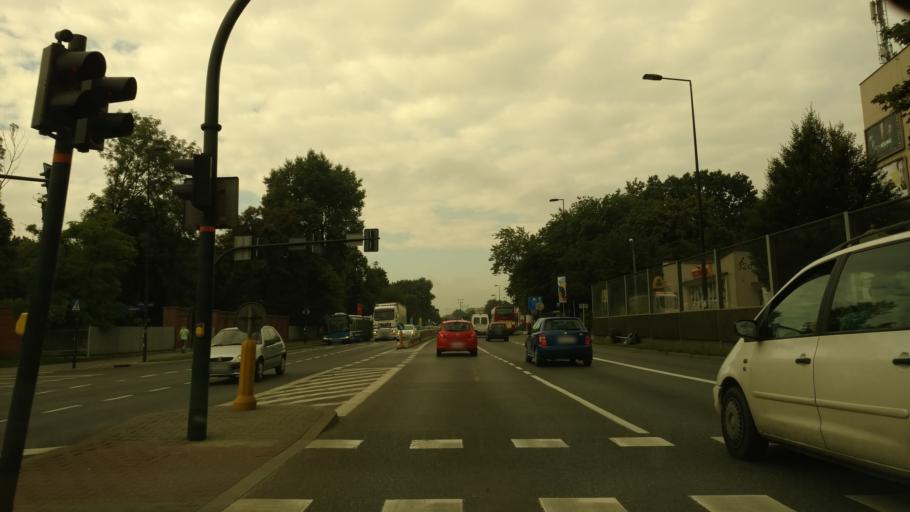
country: PL
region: Lesser Poland Voivodeship
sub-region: Krakow
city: Krakow
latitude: 50.0788
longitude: 19.9493
